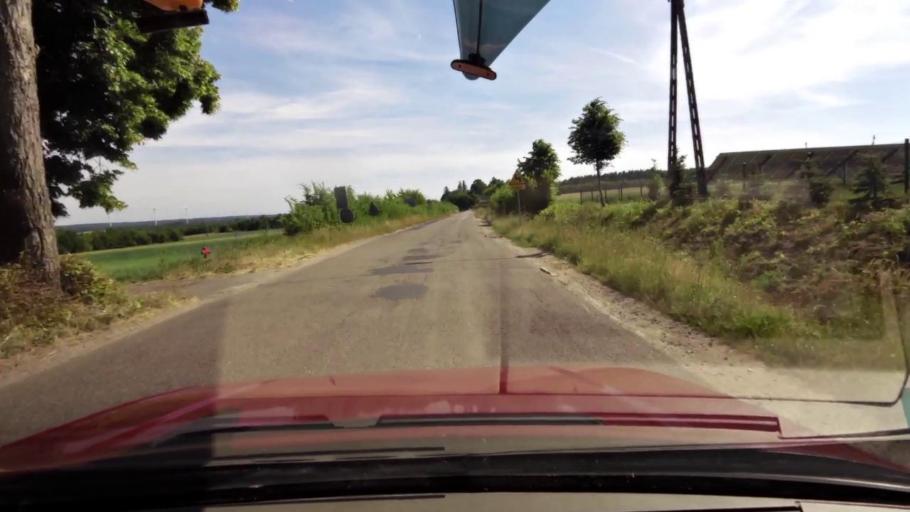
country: PL
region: Pomeranian Voivodeship
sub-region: Powiat slupski
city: Kobylnica
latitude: 54.3773
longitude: 16.9657
